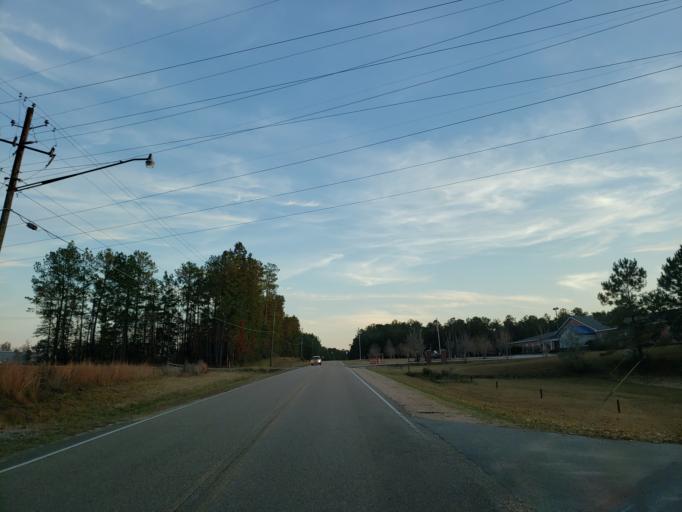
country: US
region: Mississippi
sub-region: Forrest County
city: Hattiesburg
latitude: 31.2863
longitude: -89.3116
